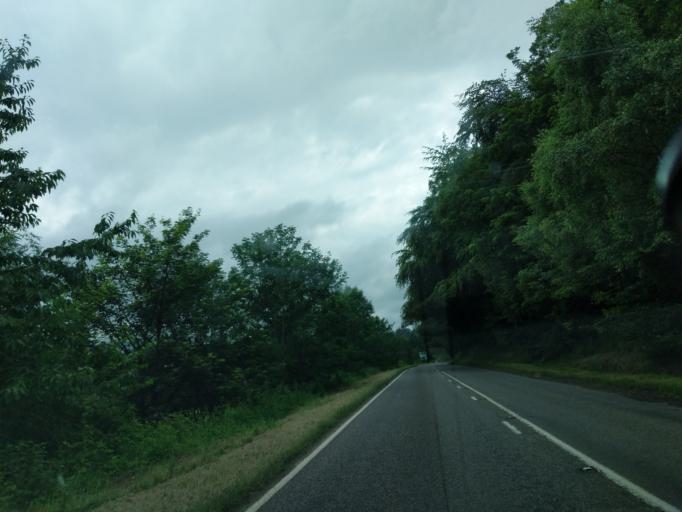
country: GB
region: Scotland
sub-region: Moray
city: Rothes
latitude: 57.4947
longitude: -3.1902
